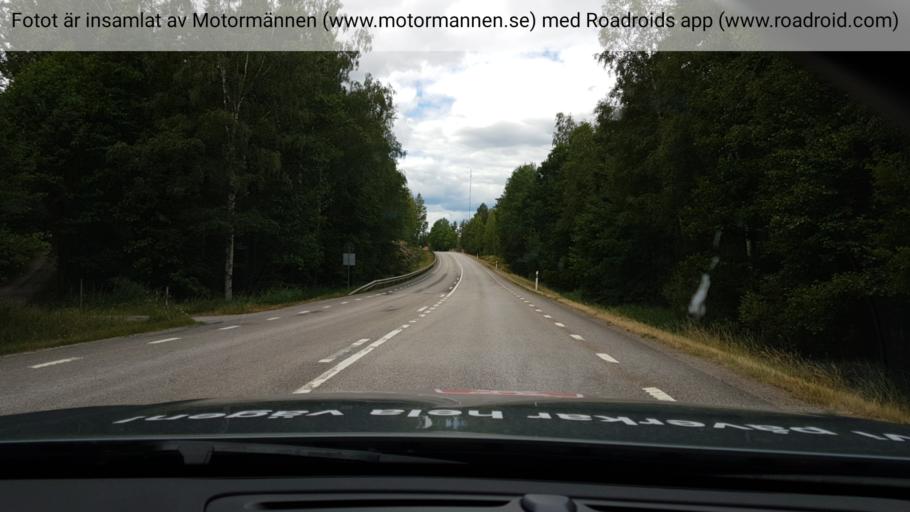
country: SE
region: Kalmar
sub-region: Vasterviks Kommun
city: Ankarsrum
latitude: 57.7224
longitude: 16.4733
